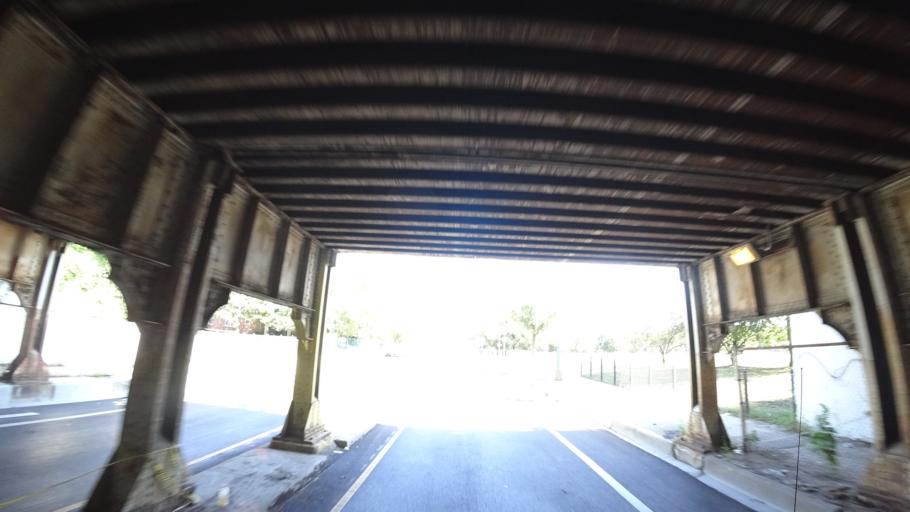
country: US
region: Illinois
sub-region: Cook County
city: Cicero
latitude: 41.8687
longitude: -87.7155
